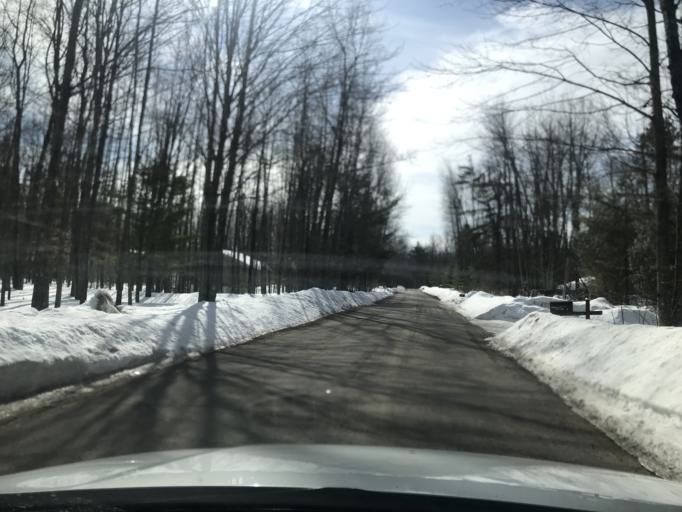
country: US
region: Wisconsin
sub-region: Menominee County
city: Legend Lake
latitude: 45.1163
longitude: -88.4439
